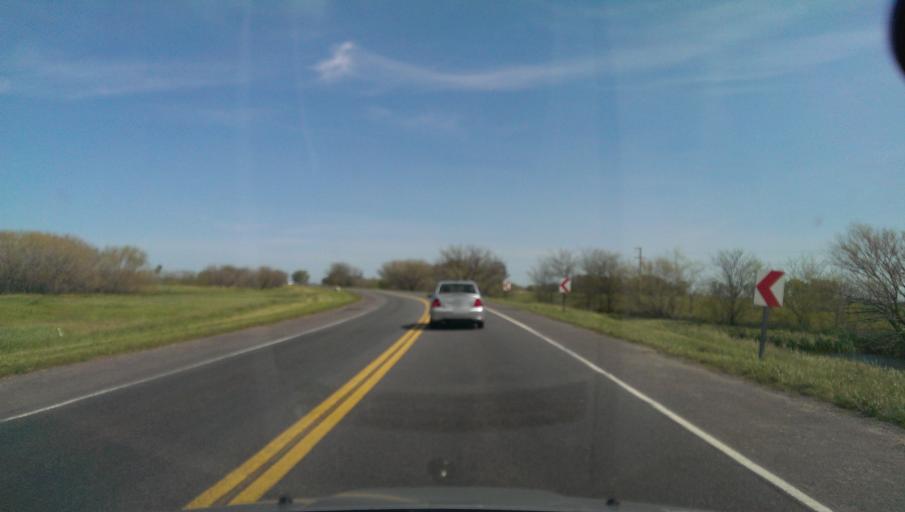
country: AR
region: Buenos Aires
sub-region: Partido de Azul
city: Azul
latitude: -36.4884
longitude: -59.5925
